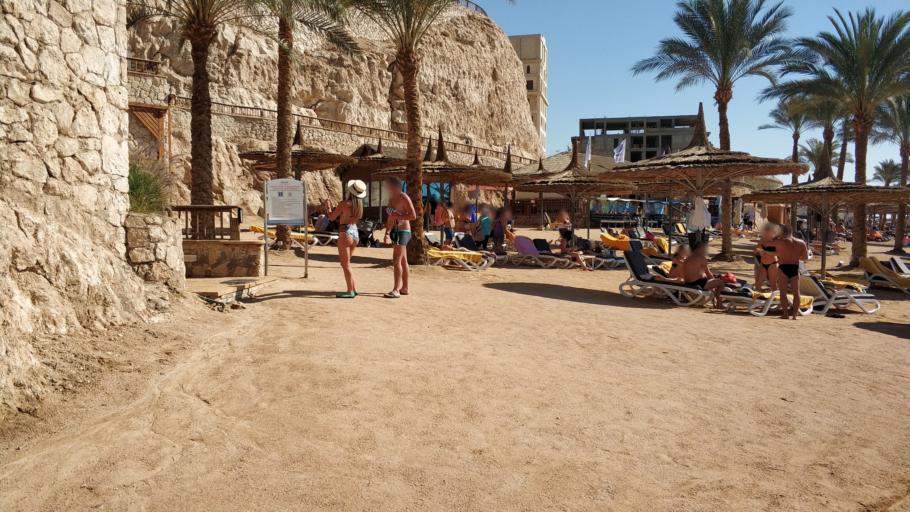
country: EG
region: South Sinai
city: Sharm el-Sheikh
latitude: 27.9152
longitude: 34.3606
